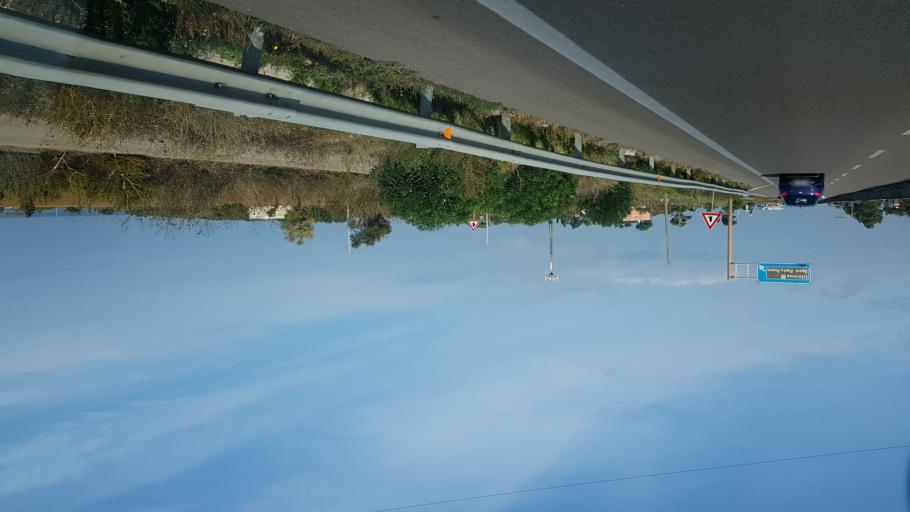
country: IT
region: Apulia
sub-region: Provincia di Brindisi
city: San Vito dei Normanni
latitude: 40.6906
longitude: 17.8223
